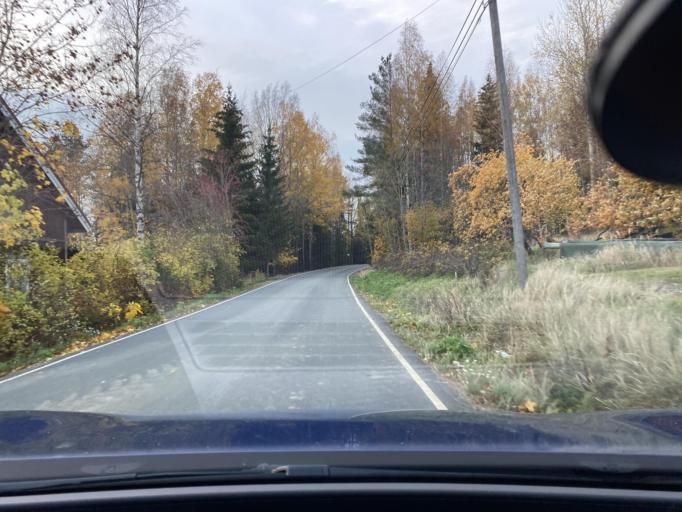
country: FI
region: Varsinais-Suomi
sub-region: Loimaa
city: Alastaro
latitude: 61.0987
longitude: 22.8946
